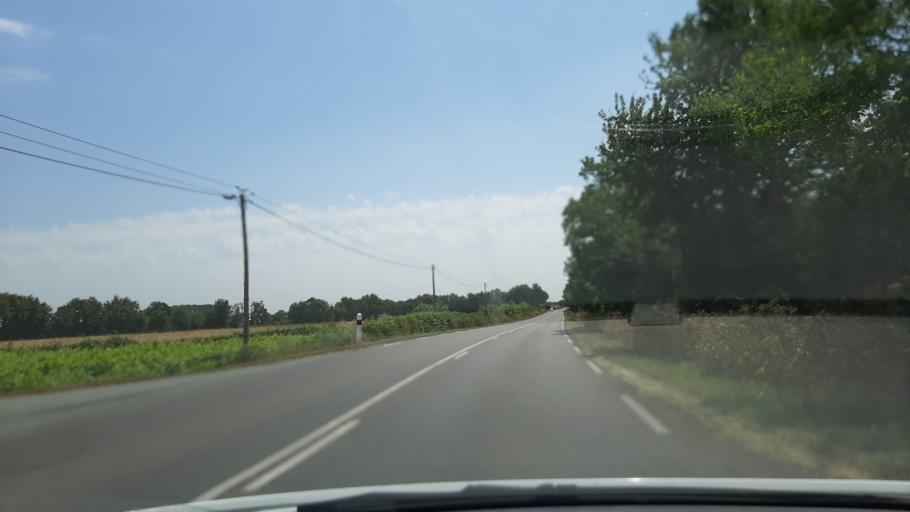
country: FR
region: Pays de la Loire
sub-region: Departement de la Vendee
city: Le Poire-sur-Vie
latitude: 46.7623
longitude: -1.4860
